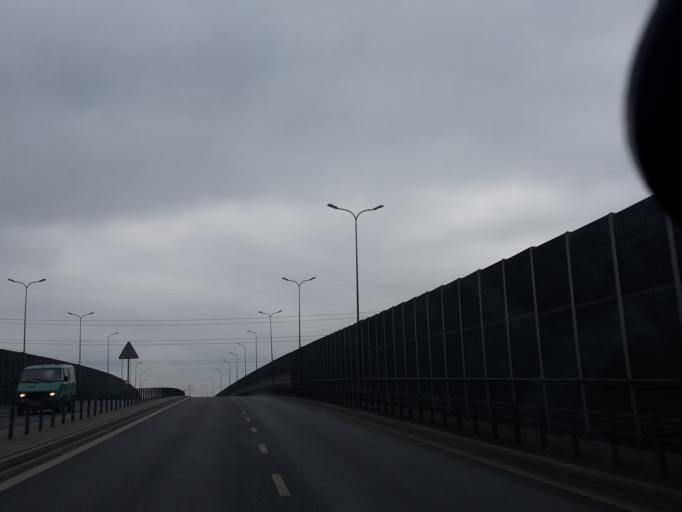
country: PL
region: Masovian Voivodeship
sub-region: Powiat warszawski zachodni
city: Lomianki
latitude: 52.3289
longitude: 20.8994
